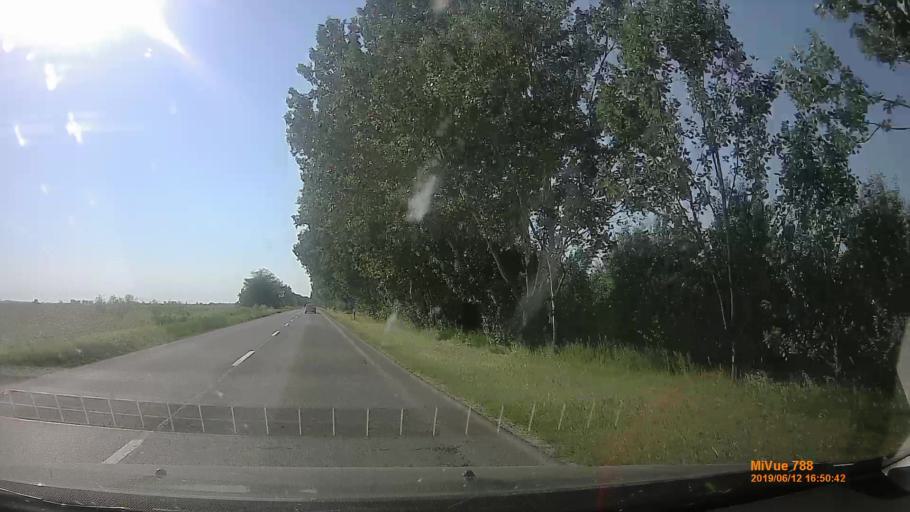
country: HU
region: Csongrad
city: Kiszombor
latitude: 46.2018
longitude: 20.3900
